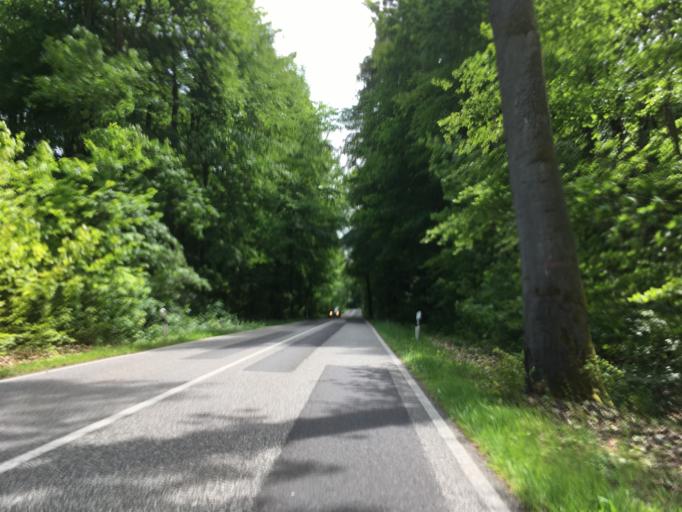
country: DE
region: Brandenburg
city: Bad Freienwalde
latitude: 52.7220
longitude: 13.9969
